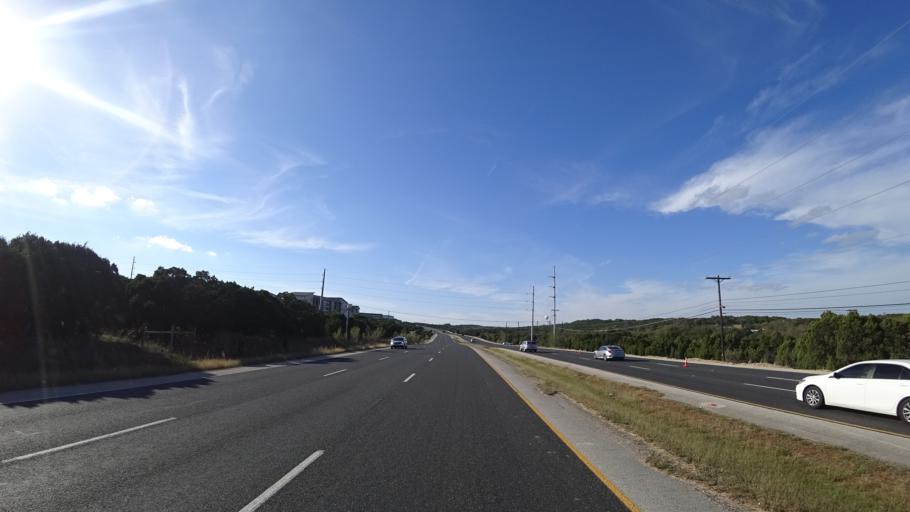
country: US
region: Texas
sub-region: Travis County
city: Barton Creek
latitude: 30.2489
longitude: -97.8516
